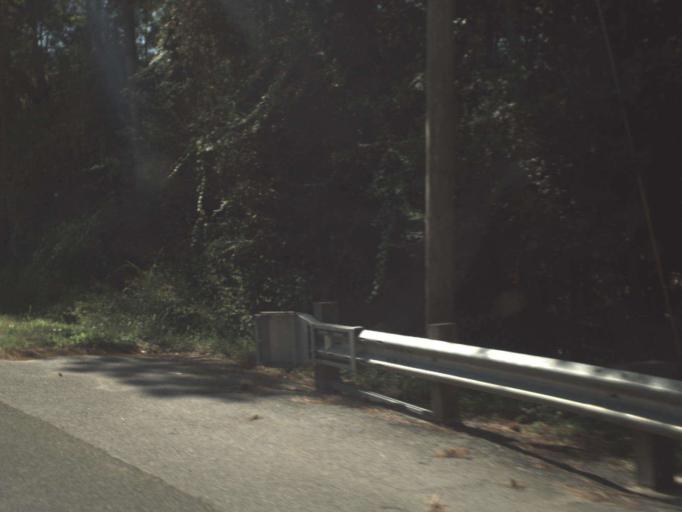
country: US
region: Florida
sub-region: Walton County
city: DeFuniak Springs
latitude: 30.7733
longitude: -86.1137
